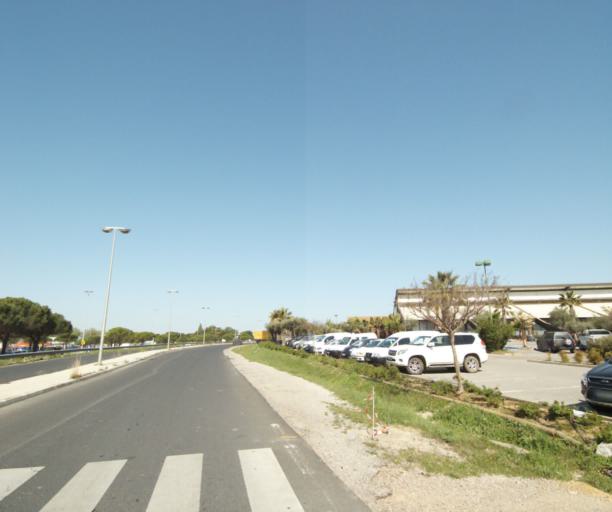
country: FR
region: Languedoc-Roussillon
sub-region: Departement de l'Herault
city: Perols
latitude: 43.5833
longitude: 3.9326
